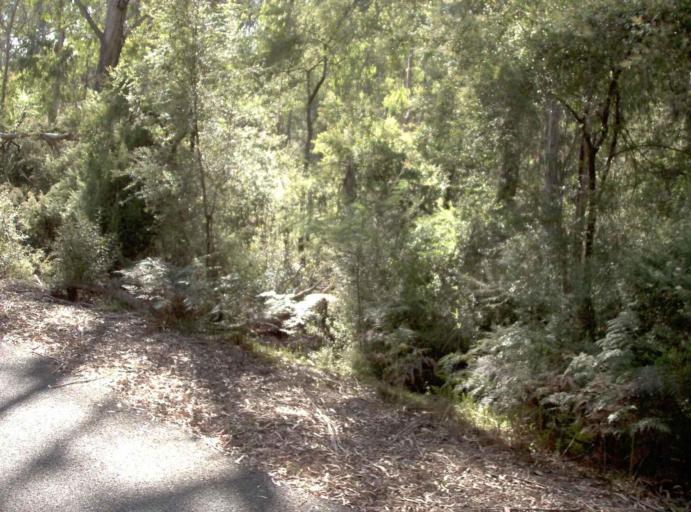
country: AU
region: Victoria
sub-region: East Gippsland
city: Lakes Entrance
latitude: -37.5030
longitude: 148.5428
